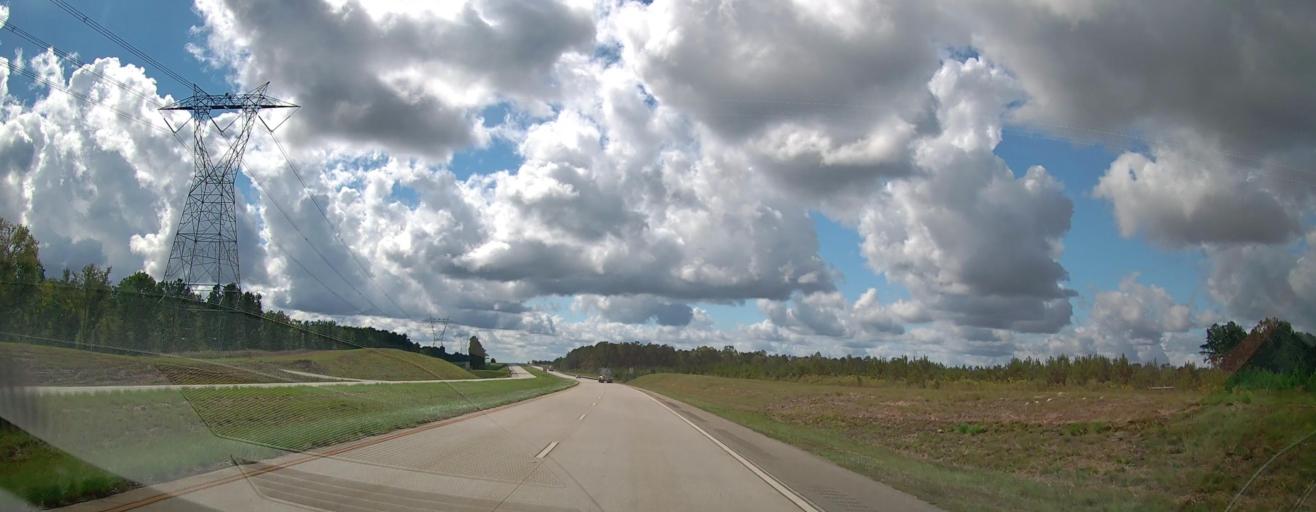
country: US
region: Georgia
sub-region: Jones County
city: Gray
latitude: 33.0273
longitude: -83.5458
